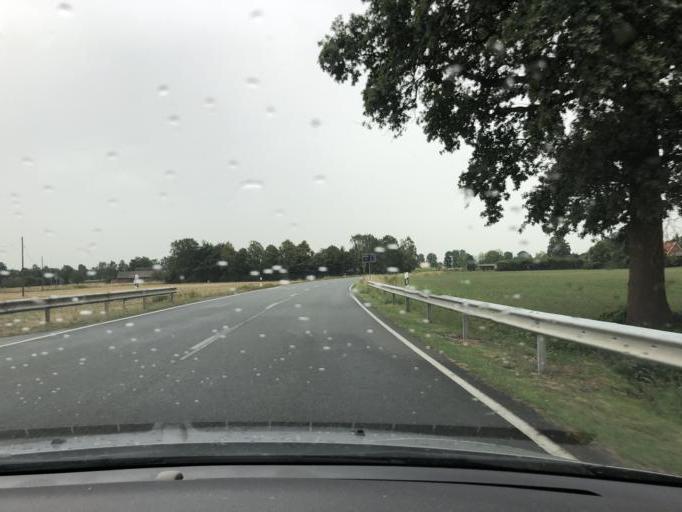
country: DE
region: North Rhine-Westphalia
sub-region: Regierungsbezirk Munster
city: Sudlohn
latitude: 51.9239
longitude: 6.8467
